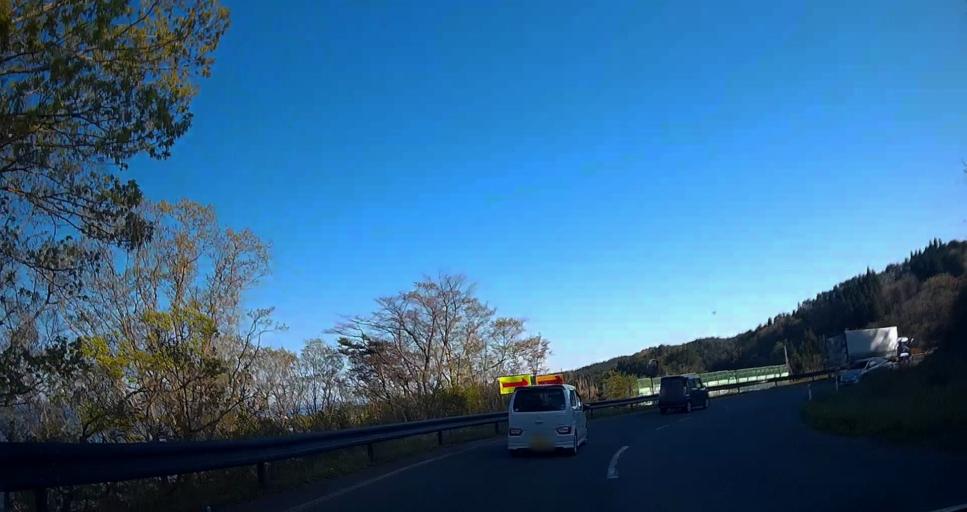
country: JP
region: Aomori
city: Mutsu
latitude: 41.4226
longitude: 141.1491
